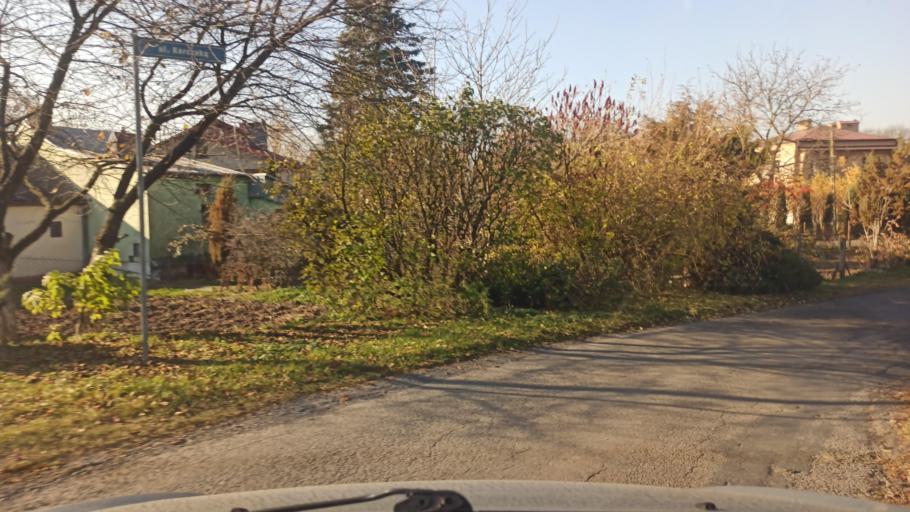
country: PL
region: Subcarpathian Voivodeship
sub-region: Powiat jaroslawski
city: Radymno
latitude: 49.9412
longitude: 22.8190
